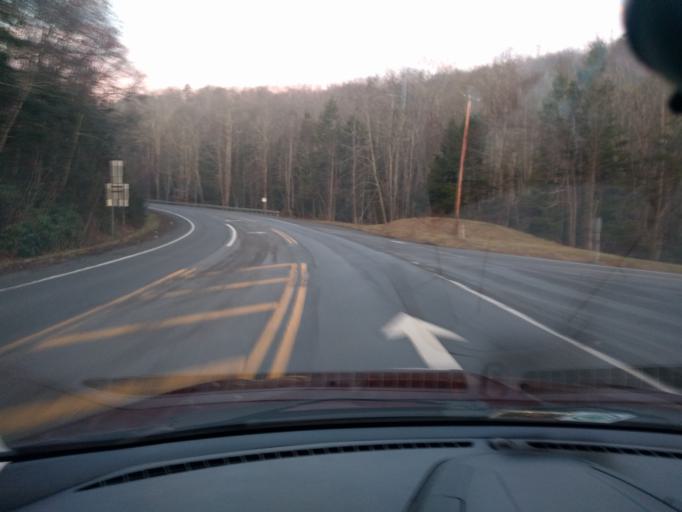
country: US
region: West Virginia
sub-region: Fayette County
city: Fayetteville
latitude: 38.0515
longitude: -80.9292
